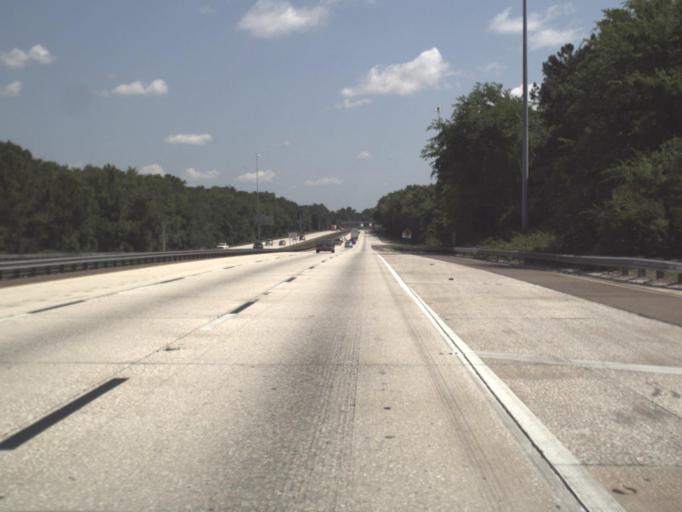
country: US
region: Florida
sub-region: Duval County
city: Jacksonville
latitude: 30.4824
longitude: -81.6433
